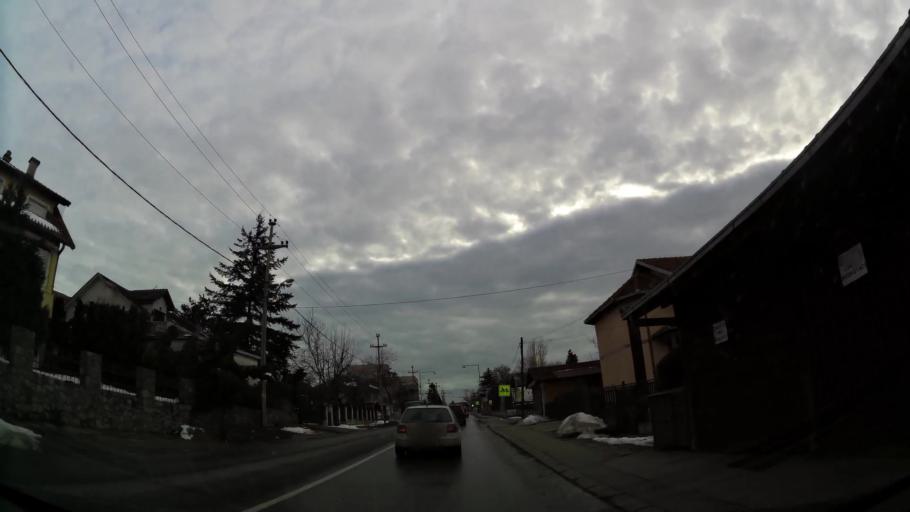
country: RS
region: Central Serbia
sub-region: Belgrade
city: Vozdovac
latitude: 44.7373
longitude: 20.4856
